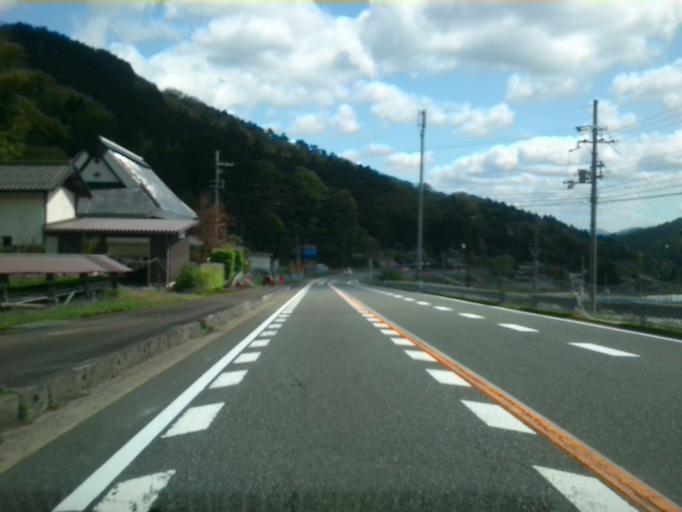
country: JP
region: Kyoto
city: Fukuchiyama
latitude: 35.3966
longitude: 135.0414
